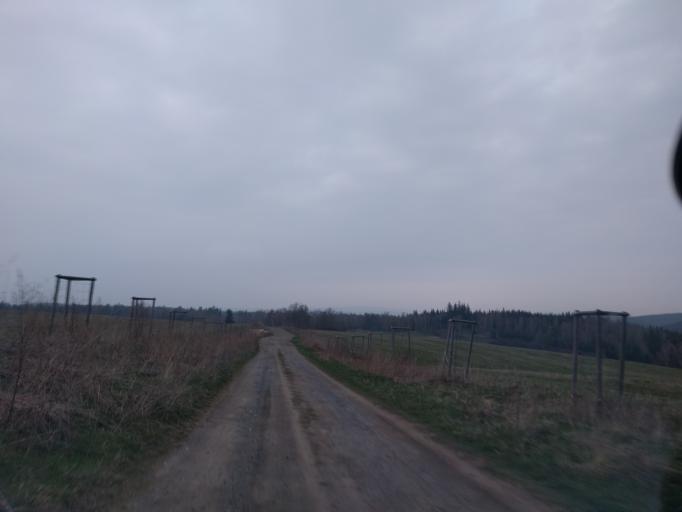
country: CZ
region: Karlovarsky
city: Bochov
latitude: 50.1002
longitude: 13.0962
